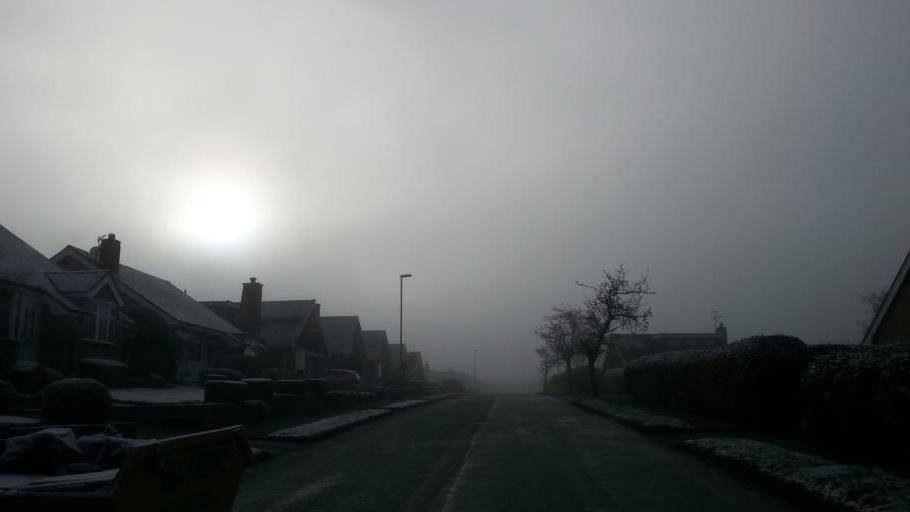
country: GB
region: England
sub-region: Staffordshire
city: Biddulph
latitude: 53.1240
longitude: -2.1583
